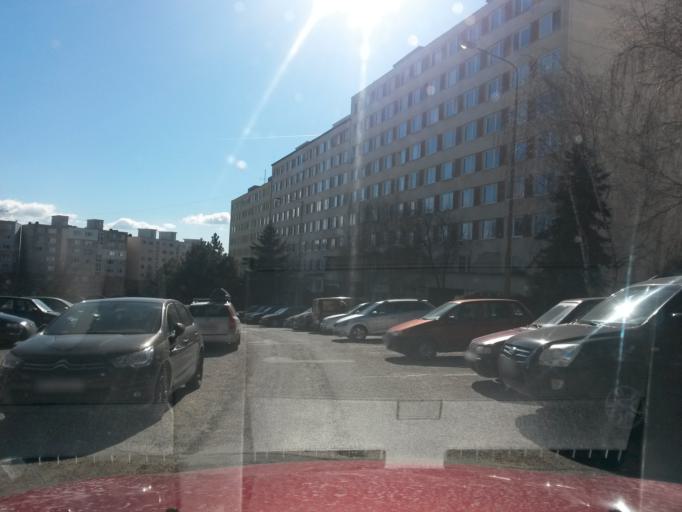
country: SK
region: Kosicky
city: Kosice
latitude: 48.7167
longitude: 21.2115
